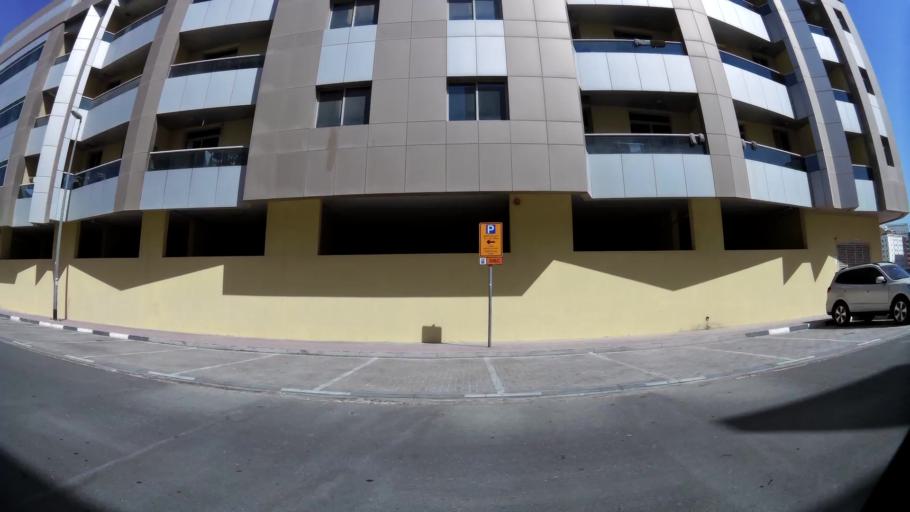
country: AE
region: Ash Shariqah
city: Sharjah
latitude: 25.2523
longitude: 55.2848
